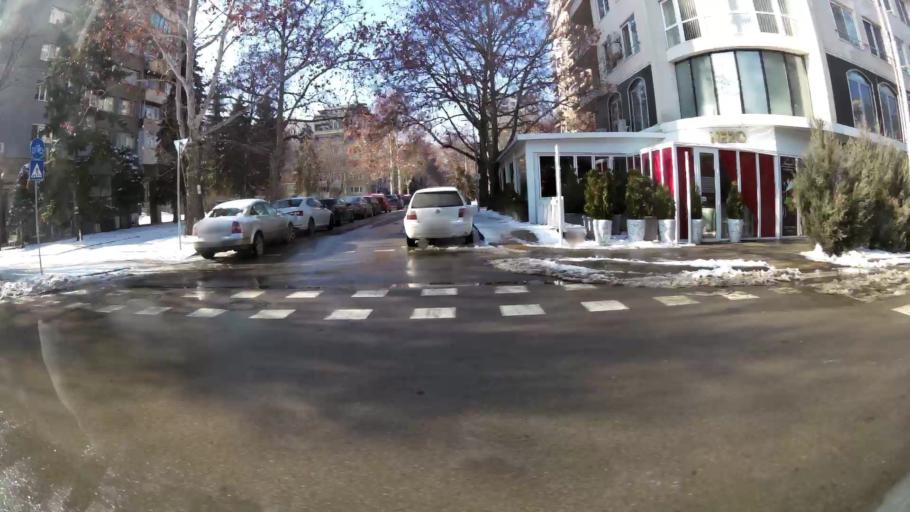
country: BG
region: Sofia-Capital
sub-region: Stolichna Obshtina
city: Sofia
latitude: 42.6775
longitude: 23.3099
